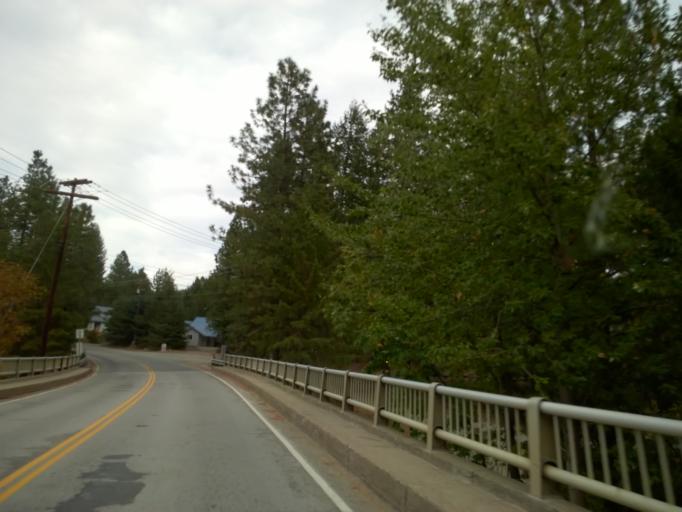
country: US
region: Washington
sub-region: Chelan County
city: Leavenworth
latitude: 47.5775
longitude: -120.6740
